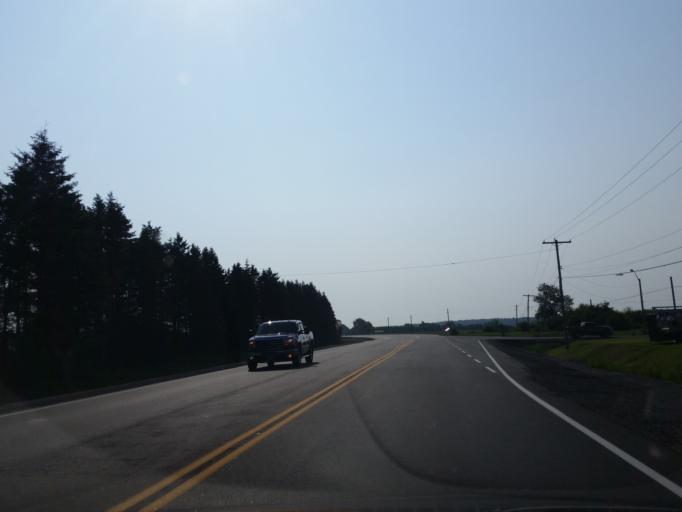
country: CA
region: Ontario
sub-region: Nipissing District
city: North Bay
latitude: 46.4077
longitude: -80.1000
